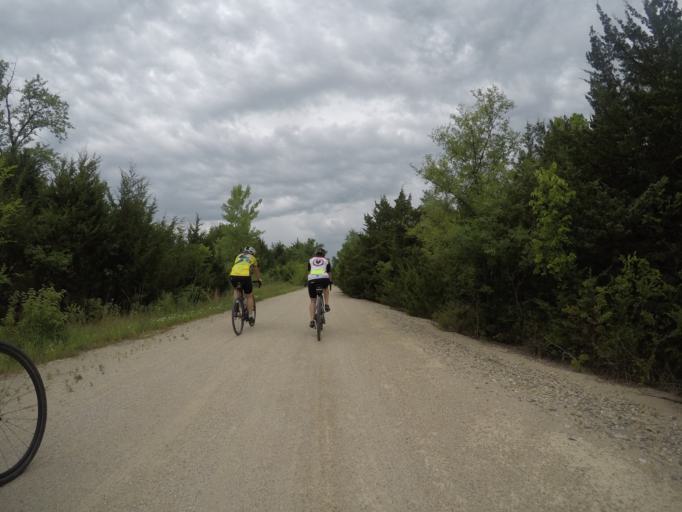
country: US
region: Kansas
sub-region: Anderson County
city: Garnett
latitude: 38.2651
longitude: -95.2459
